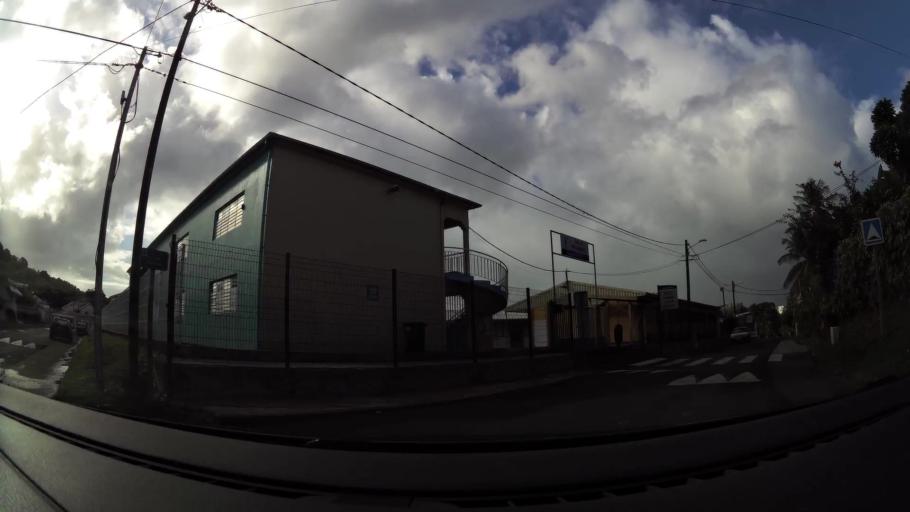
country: GP
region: Guadeloupe
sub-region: Guadeloupe
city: Les Abymes
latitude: 16.2524
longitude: -61.5113
